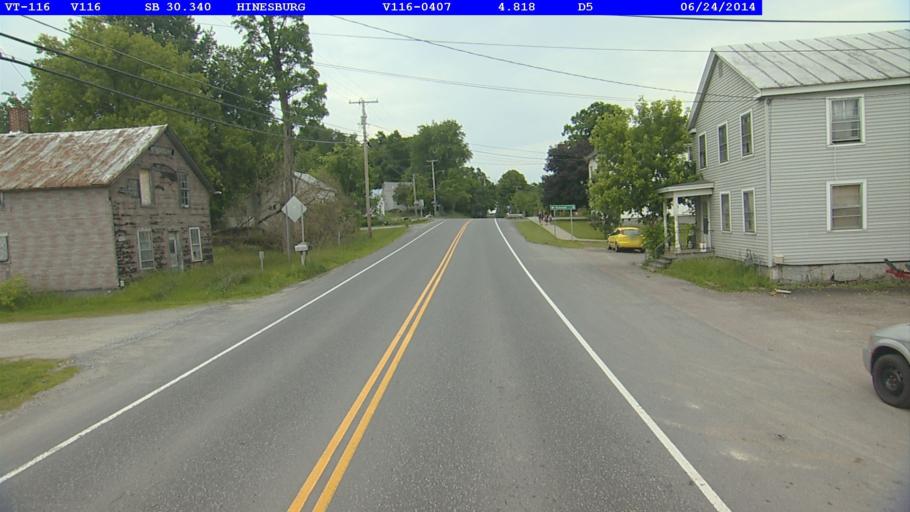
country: US
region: Vermont
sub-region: Chittenden County
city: Hinesburg
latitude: 44.3327
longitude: -73.1113
